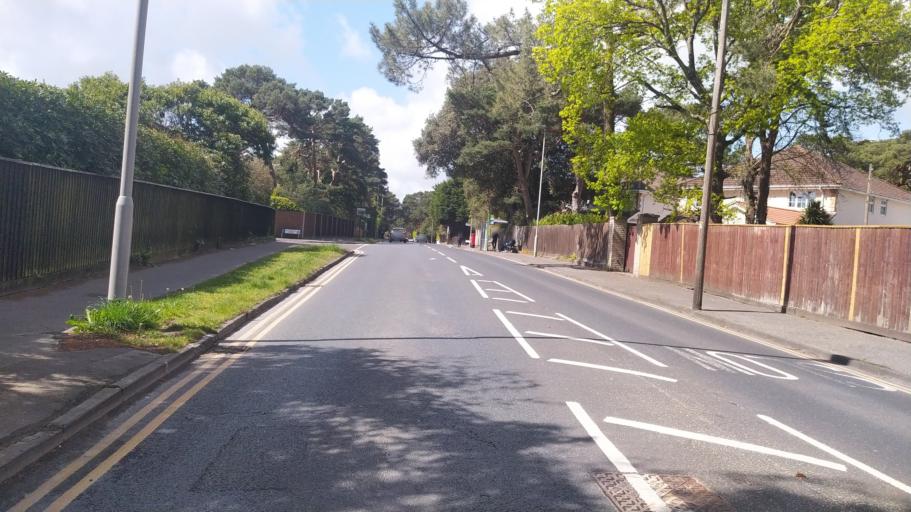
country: GB
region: England
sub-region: Dorset
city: Parkstone
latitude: 50.7005
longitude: -1.9270
